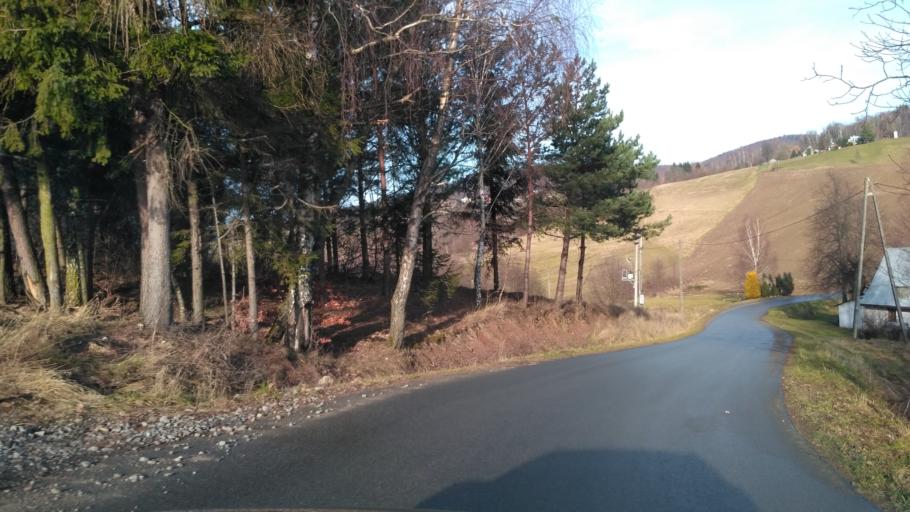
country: PL
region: Subcarpathian Voivodeship
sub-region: Powiat krosnienski
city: Korczyna
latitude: 49.7327
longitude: 21.7852
